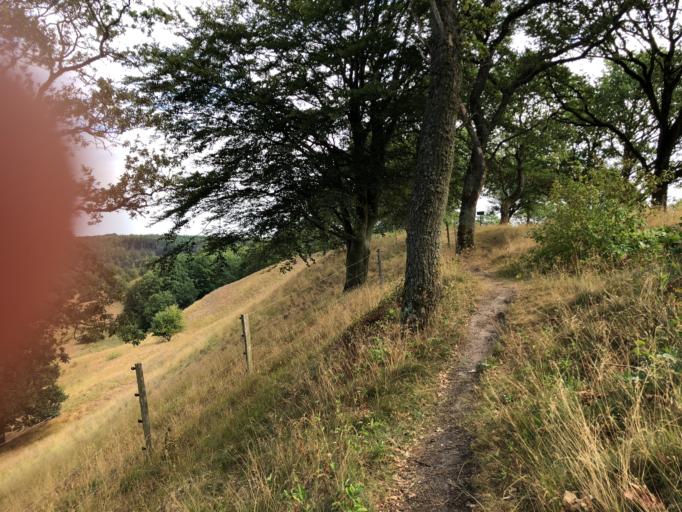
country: DK
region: South Denmark
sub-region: Vejle Kommune
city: Egtved
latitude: 55.6534
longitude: 9.2880
